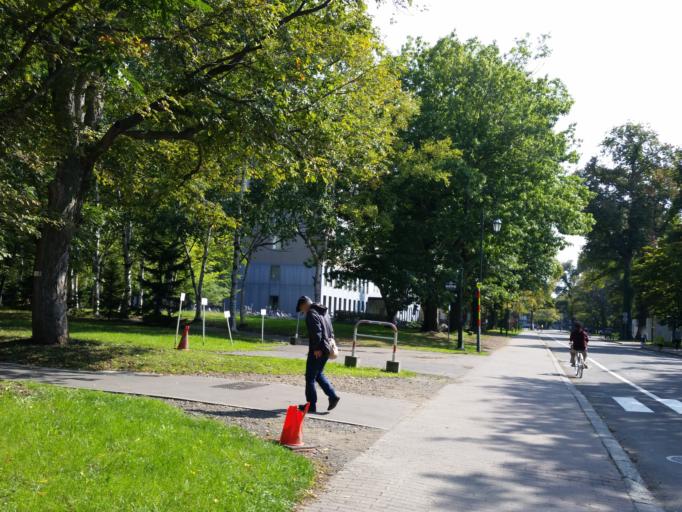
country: JP
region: Hokkaido
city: Sapporo
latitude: 43.0734
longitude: 141.3424
